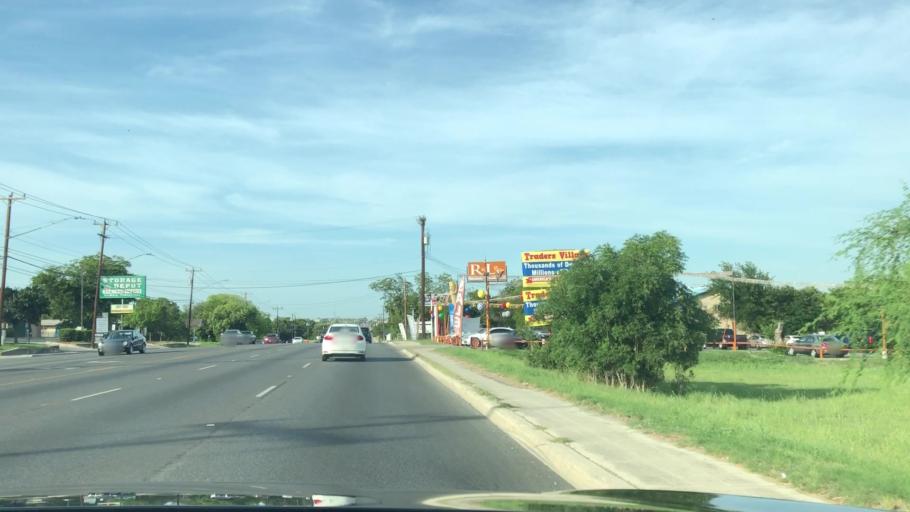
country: US
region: Texas
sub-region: Bexar County
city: Leon Valley
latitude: 29.5258
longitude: -98.5977
